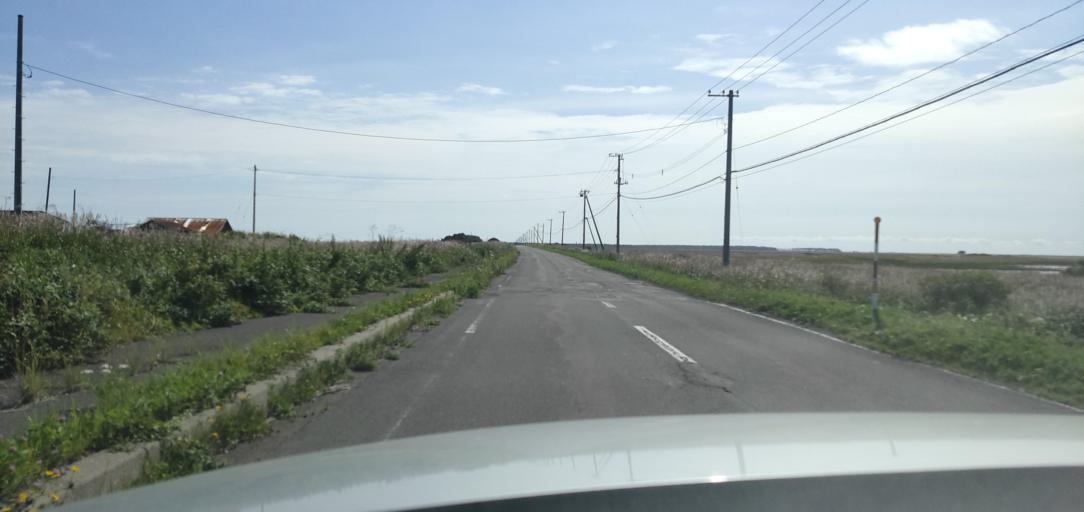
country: JP
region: Hokkaido
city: Shibetsu
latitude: 43.6203
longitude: 145.2263
